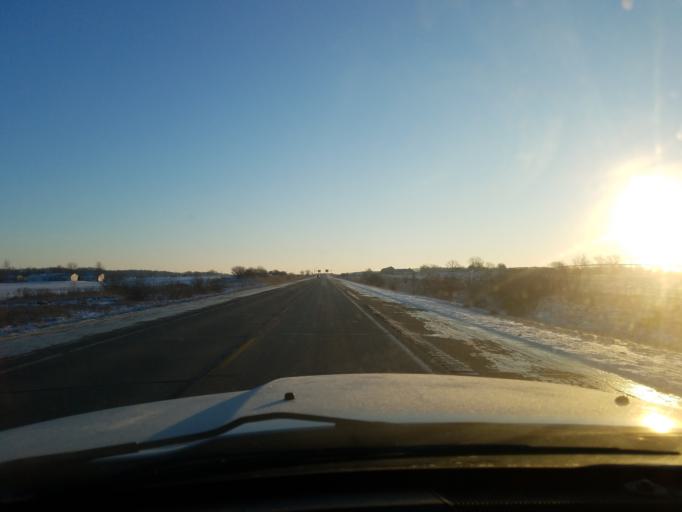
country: US
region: Indiana
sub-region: Marshall County
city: Bremen
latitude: 41.4606
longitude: -86.1706
